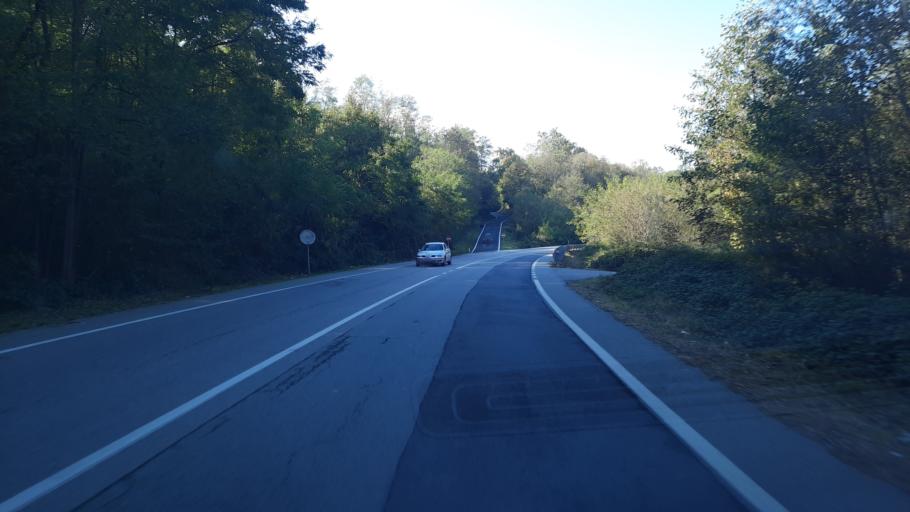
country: IT
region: Piedmont
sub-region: Provincia di Novara
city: Gozzano
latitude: 45.7391
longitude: 8.4283
